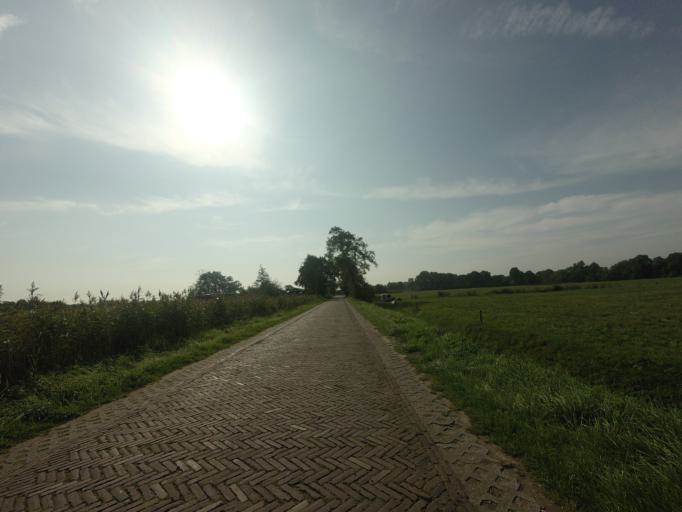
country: NL
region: Groningen
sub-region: Gemeente Leek
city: Leek
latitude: 53.1694
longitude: 6.4111
